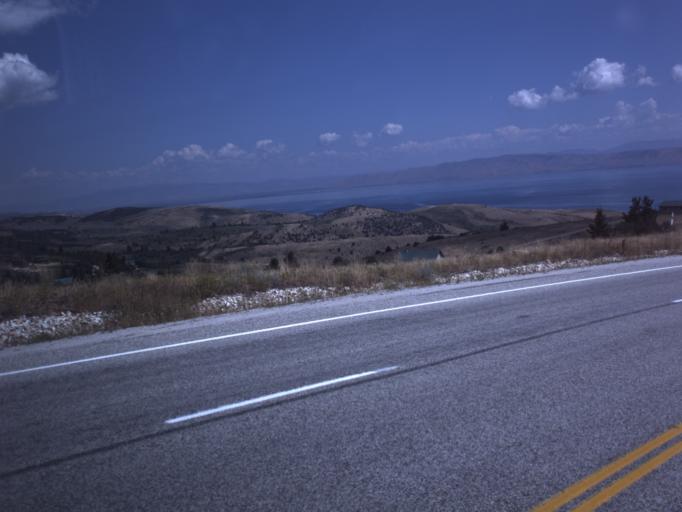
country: US
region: Idaho
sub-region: Bear Lake County
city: Paris
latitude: 41.9317
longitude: -111.4361
